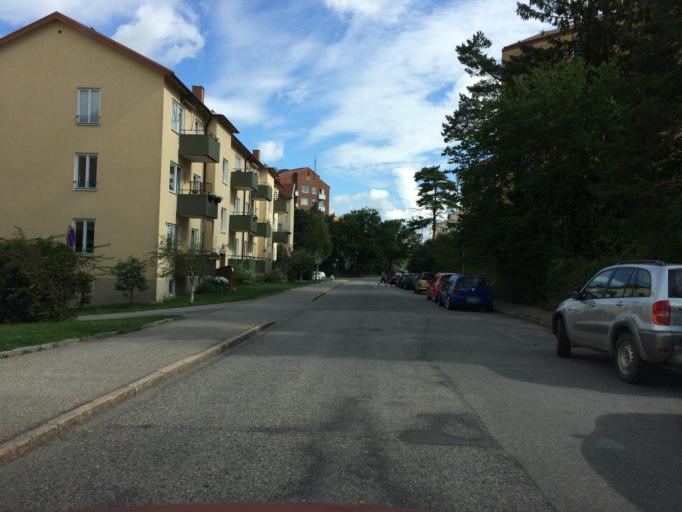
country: SE
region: Stockholm
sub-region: Huddinge Kommun
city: Segeltorp
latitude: 59.2989
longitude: 17.9797
